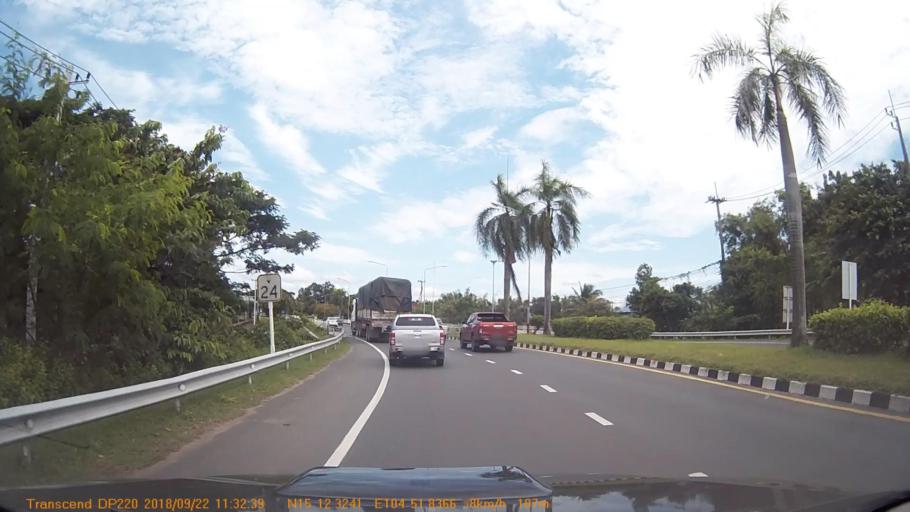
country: TH
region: Changwat Ubon Ratchathani
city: Warin Chamrap
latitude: 15.2055
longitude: 104.8640
